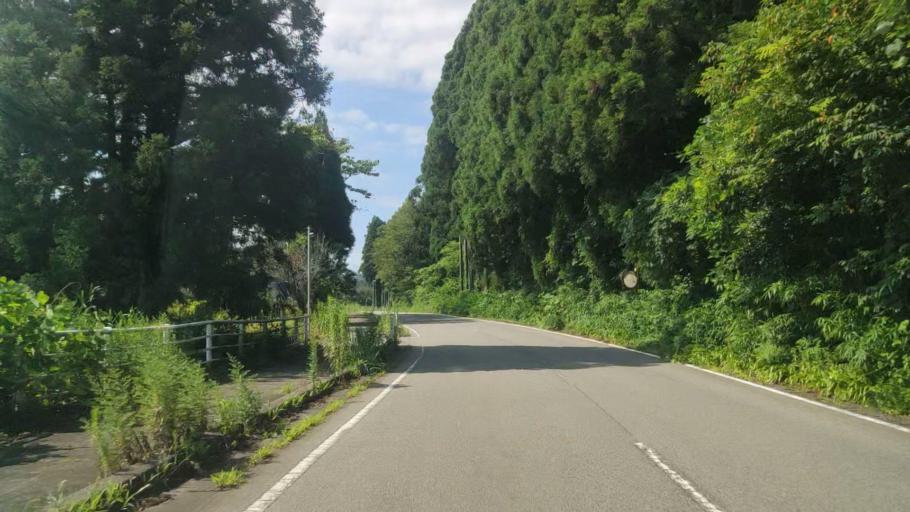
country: JP
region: Ishikawa
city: Komatsu
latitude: 36.3644
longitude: 136.4951
